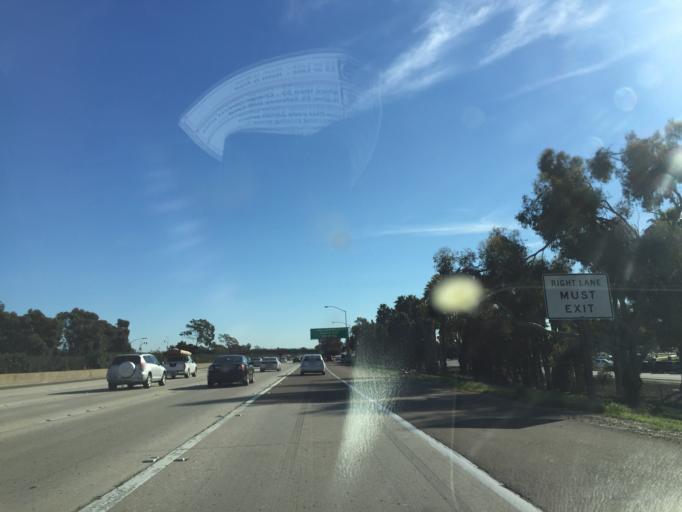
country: US
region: California
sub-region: San Diego County
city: San Diego
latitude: 32.7738
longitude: -117.2078
